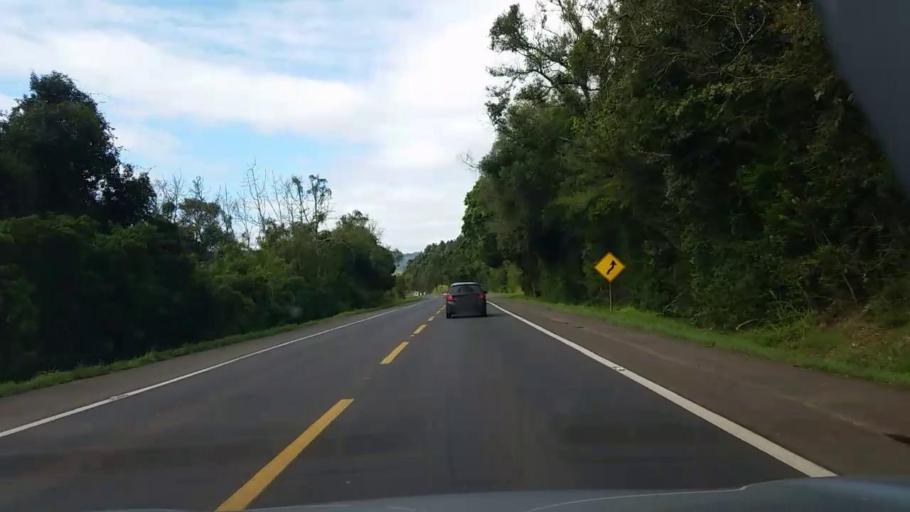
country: BR
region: Rio Grande do Sul
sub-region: Arroio Do Meio
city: Arroio do Meio
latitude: -29.3364
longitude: -52.0861
